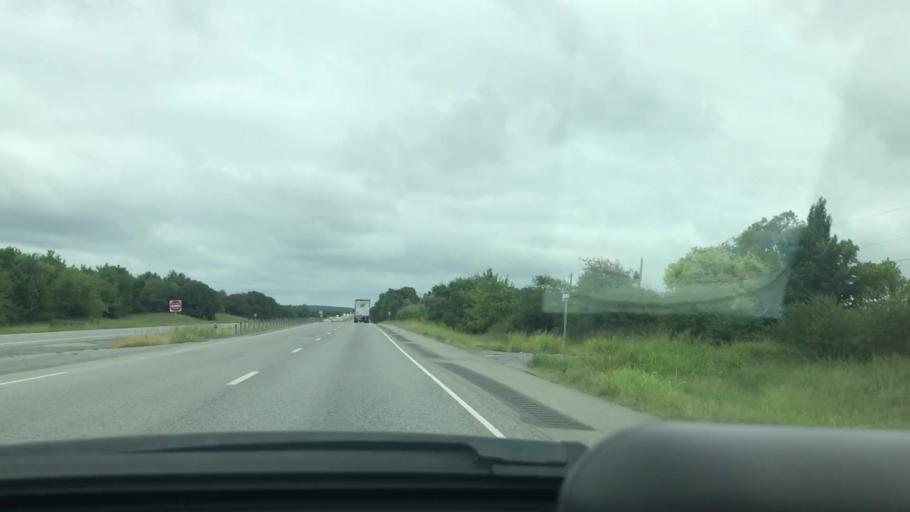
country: US
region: Oklahoma
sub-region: Pittsburg County
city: McAlester
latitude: 34.7615
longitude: -95.8900
